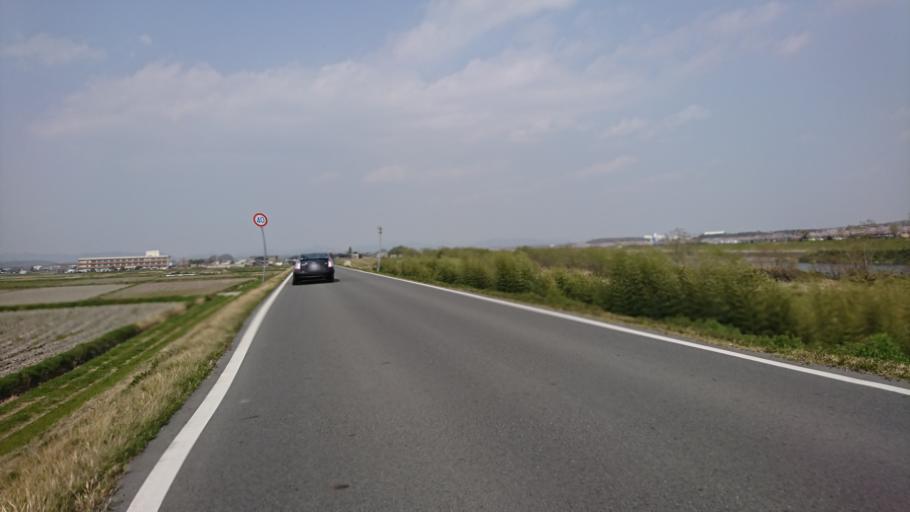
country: JP
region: Hyogo
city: Ono
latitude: 34.8653
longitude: 134.9170
